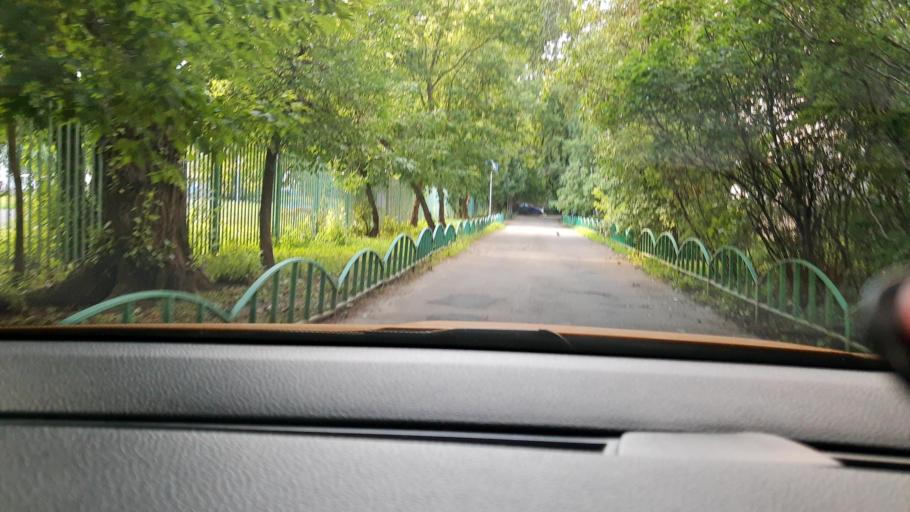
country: RU
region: Moscow
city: Mar'ino
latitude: 55.6504
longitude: 37.7223
